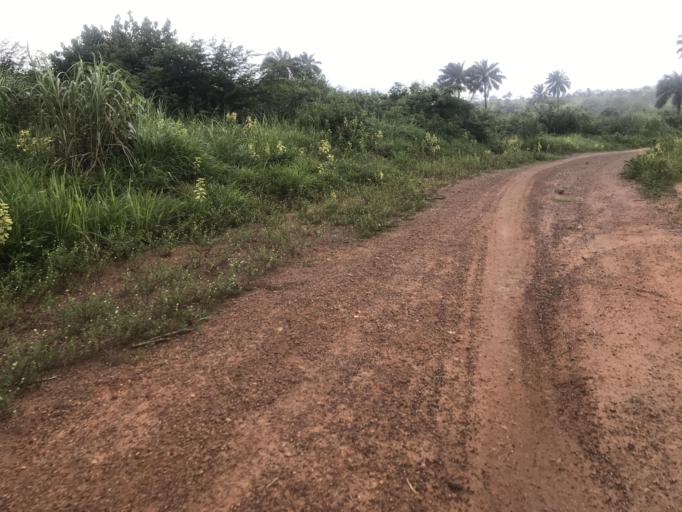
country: GN
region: Nzerekore
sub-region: Prefecture de Guekedou
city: Gueckedou
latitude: 8.4784
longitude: -10.2950
